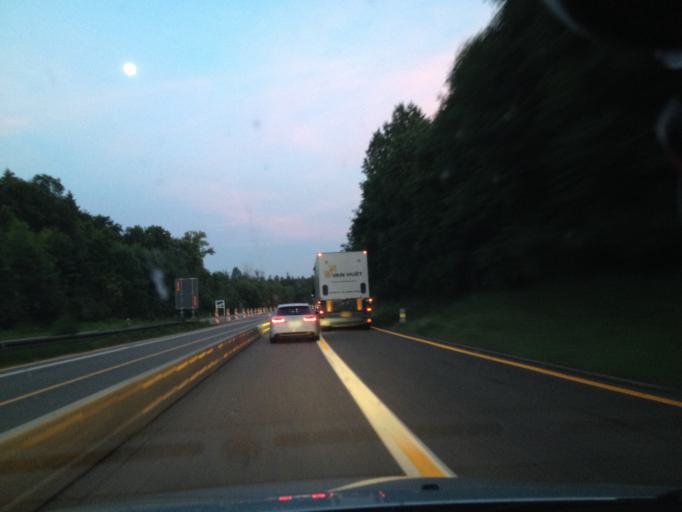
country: DE
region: Baden-Wuerttemberg
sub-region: Regierungsbezirk Stuttgart
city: Nattheim
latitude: 48.6620
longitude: 10.2320
